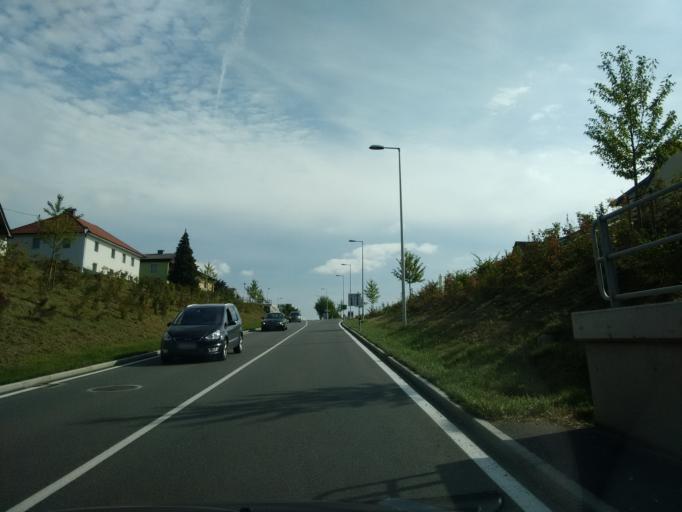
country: AT
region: Upper Austria
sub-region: Politischer Bezirk Steyr-Land
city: Bad Hall
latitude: 48.0684
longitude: 14.1904
